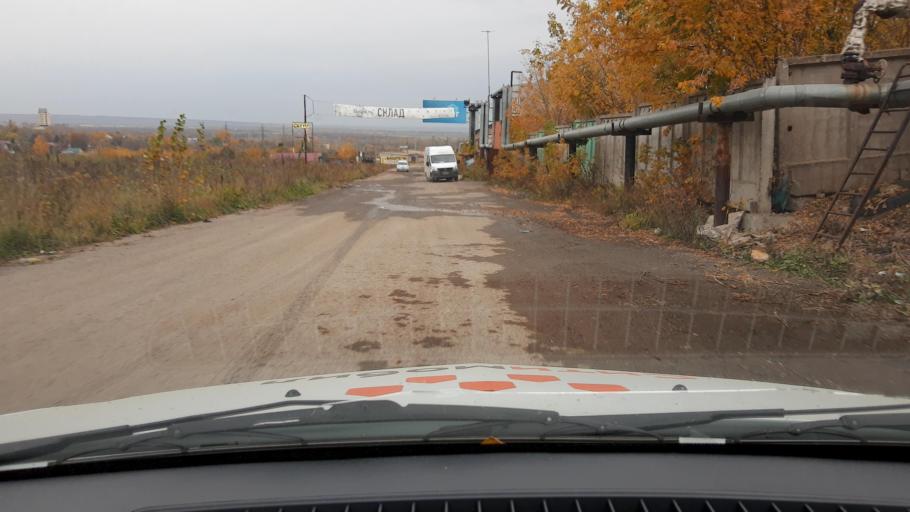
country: RU
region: Bashkortostan
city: Ufa
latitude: 54.8298
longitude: 56.0833
